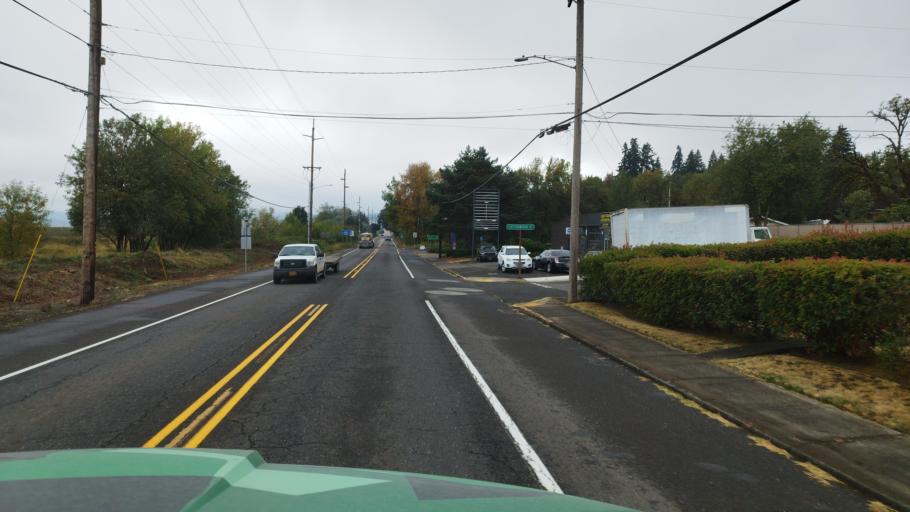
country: US
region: Oregon
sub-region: Washington County
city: Forest Grove
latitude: 45.4342
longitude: -123.1393
